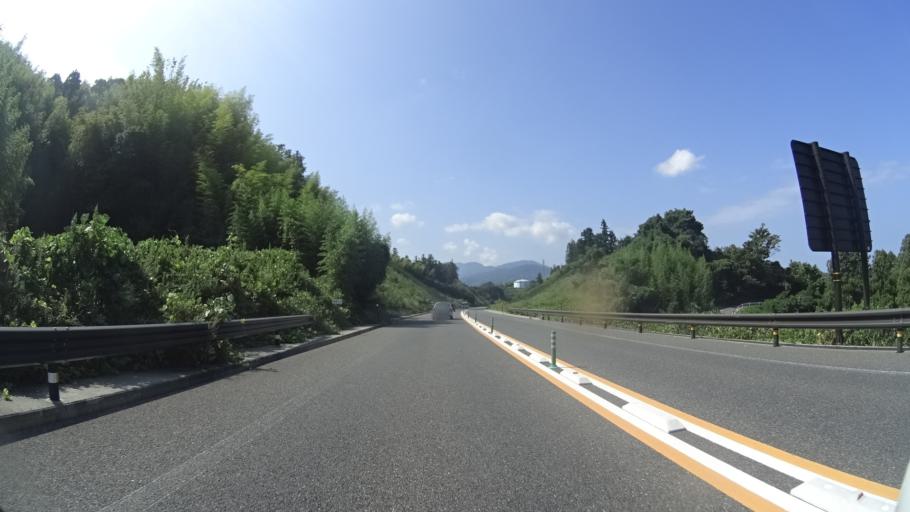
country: JP
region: Shimane
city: Hamada
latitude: 34.8676
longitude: 132.0647
